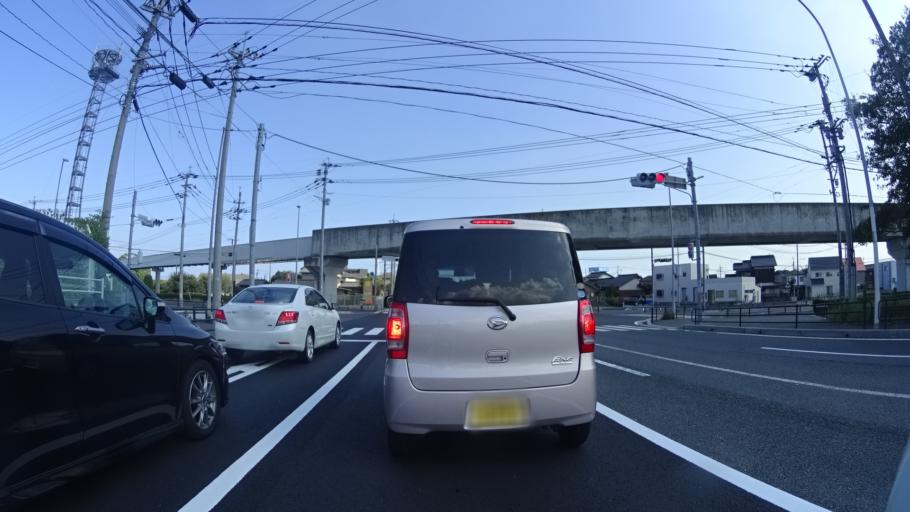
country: JP
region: Fukuoka
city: Kanda
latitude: 33.7958
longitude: 130.9783
